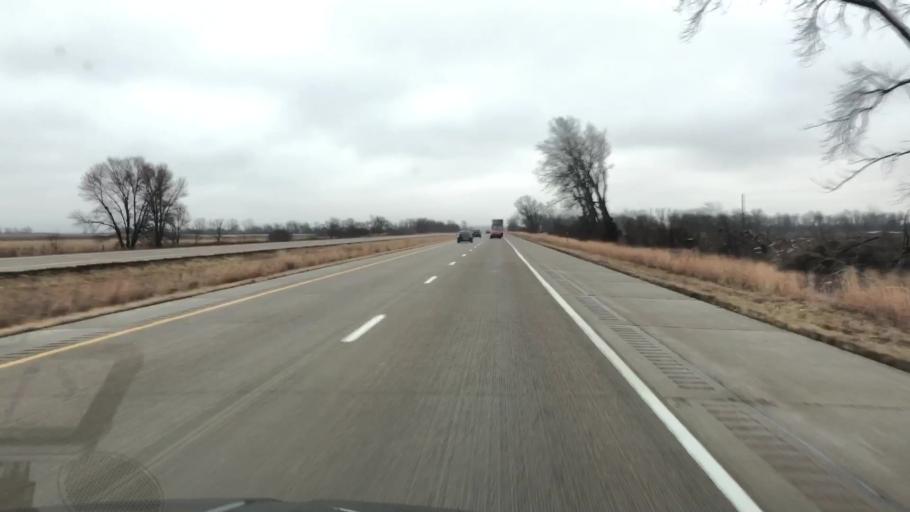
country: US
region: Nebraska
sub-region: Burt County
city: Tekamah
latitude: 41.8486
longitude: -96.0975
